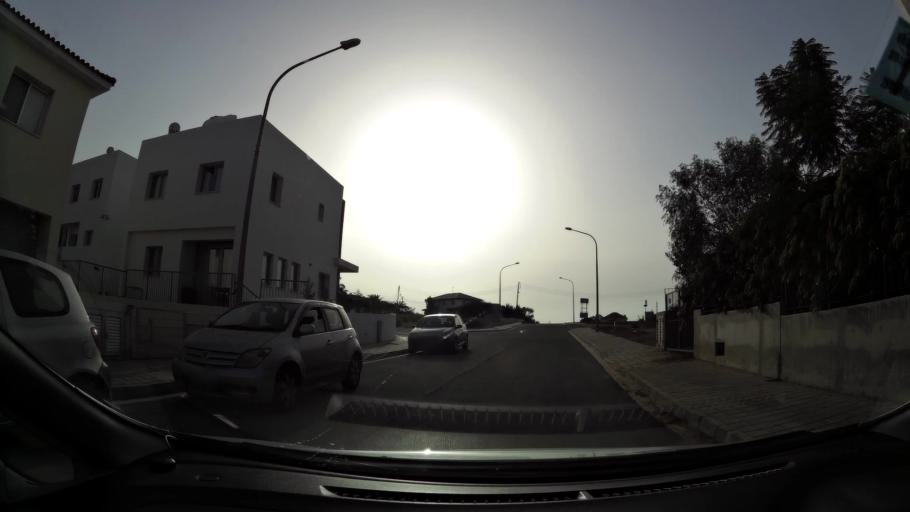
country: CY
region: Lefkosia
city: Dali
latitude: 35.0632
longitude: 33.3829
